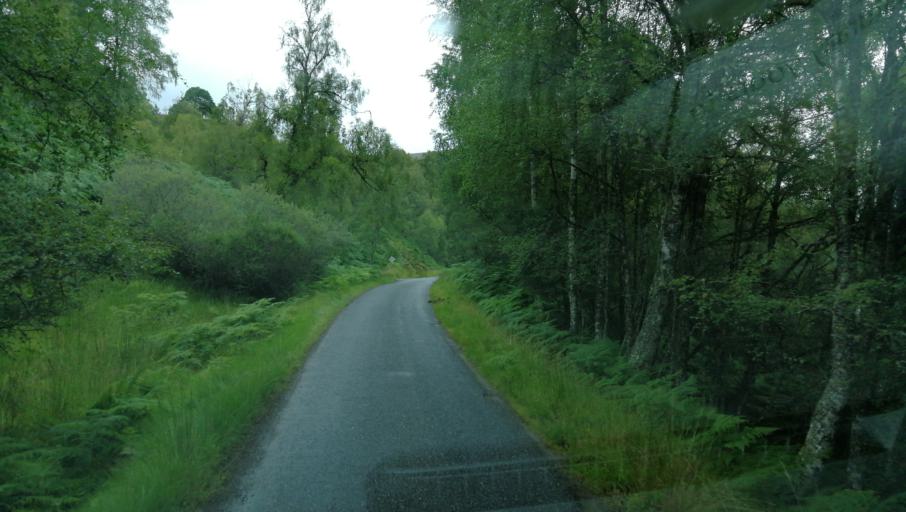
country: GB
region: Scotland
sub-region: Highland
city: Spean Bridge
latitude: 57.2860
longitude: -4.9218
